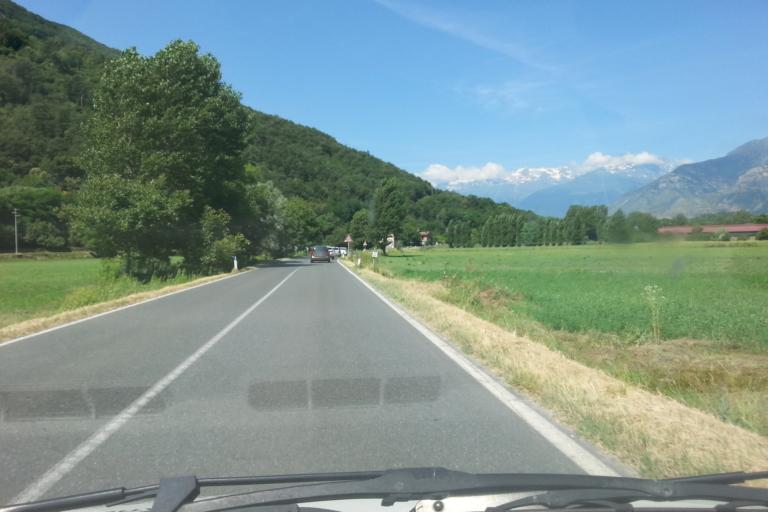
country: IT
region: Piedmont
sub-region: Provincia di Torino
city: San Didero
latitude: 45.1189
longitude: 7.2166
